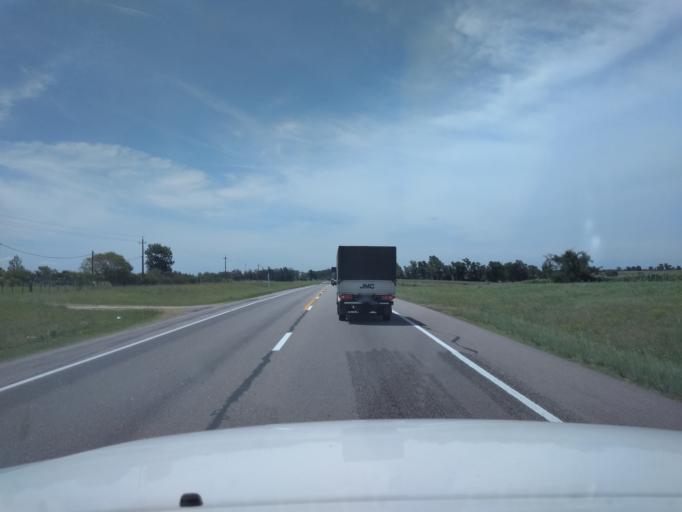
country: UY
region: Florida
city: Florida
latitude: -34.1381
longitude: -56.1826
